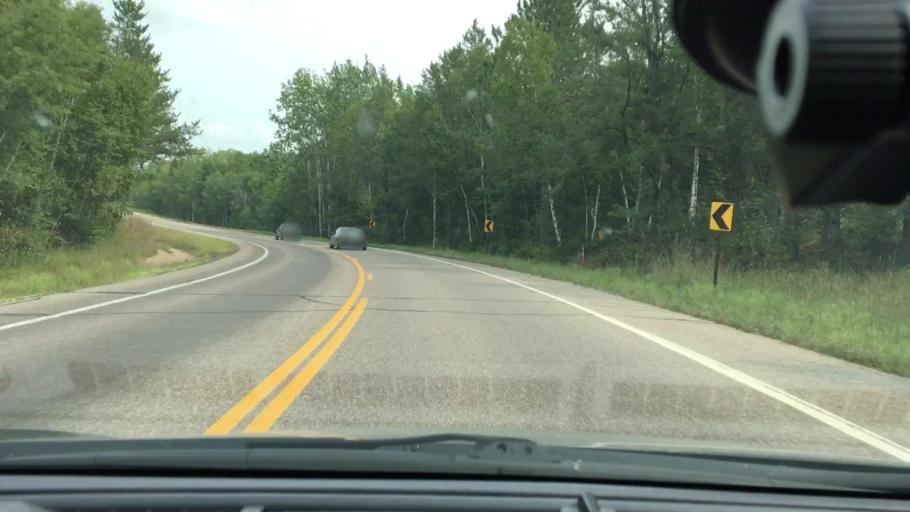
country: US
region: Minnesota
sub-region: Crow Wing County
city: Cross Lake
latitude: 46.7313
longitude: -94.0278
